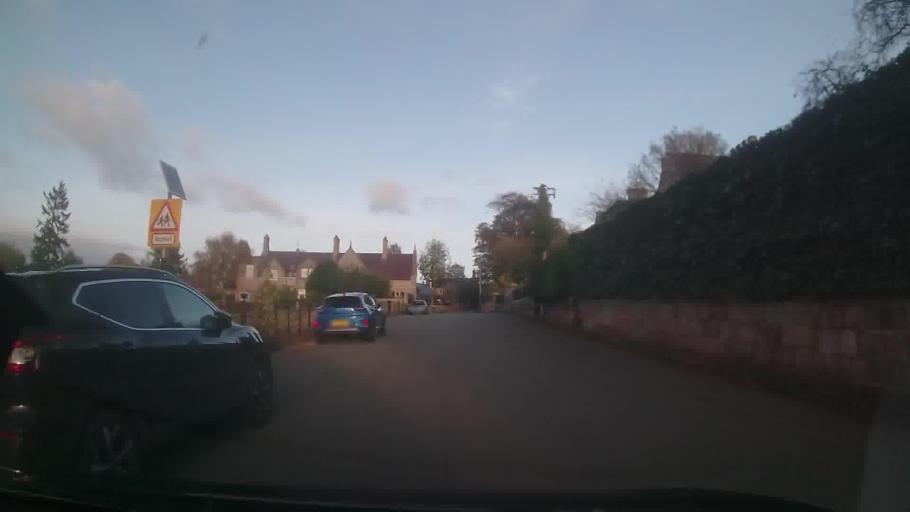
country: GB
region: England
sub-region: Shropshire
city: Clive
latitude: 52.8140
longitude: -2.7221
